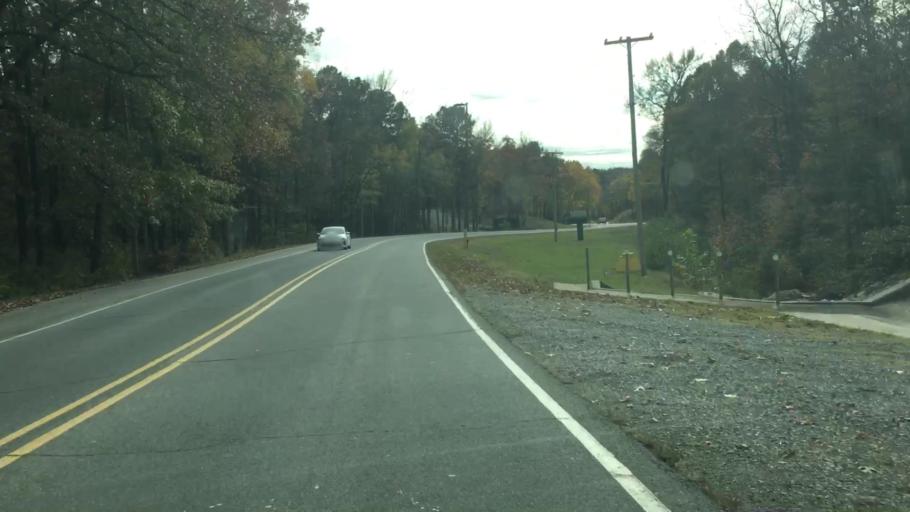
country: US
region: Arkansas
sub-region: Pulaski County
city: North Little Rock
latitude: 34.8187
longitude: -92.2887
